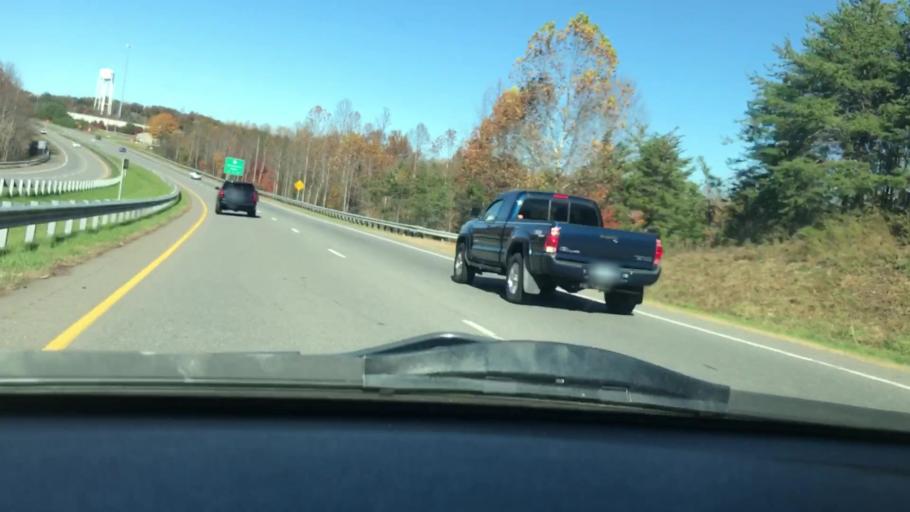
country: US
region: North Carolina
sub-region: Rockingham County
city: Stoneville
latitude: 36.4567
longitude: -79.9271
